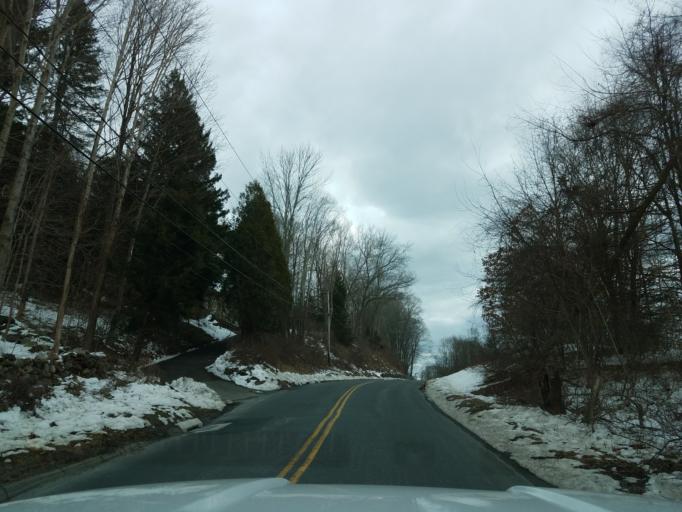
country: US
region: Connecticut
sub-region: Litchfield County
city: New Milford
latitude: 41.6004
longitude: -73.4276
